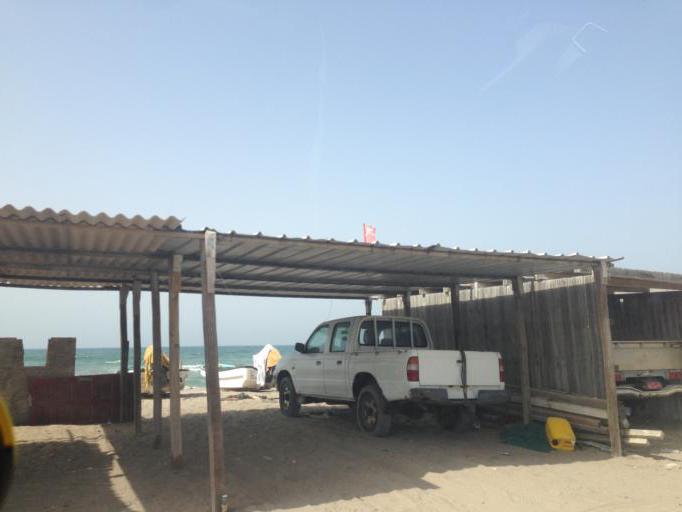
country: OM
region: Al Batinah
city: Barka'
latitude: 23.7077
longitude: 57.9324
